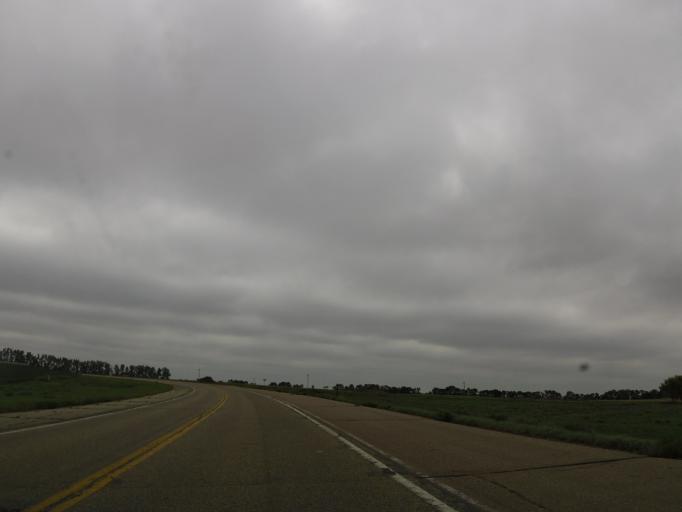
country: US
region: South Dakota
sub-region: Deuel County
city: Clear Lake
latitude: 44.9325
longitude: -96.6765
